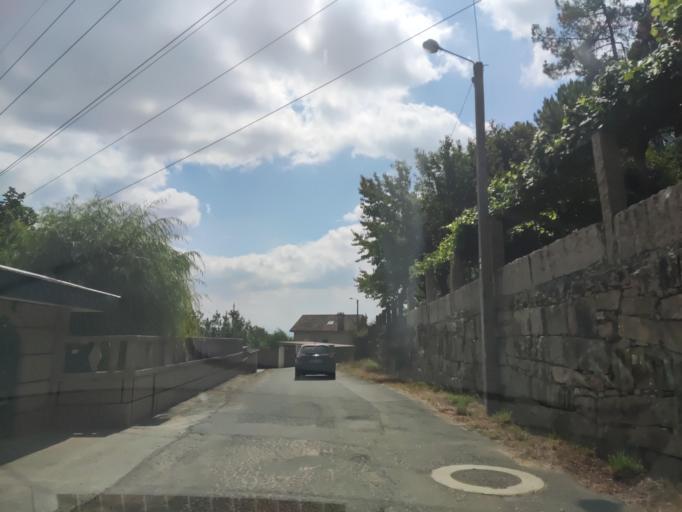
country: ES
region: Galicia
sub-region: Provincia de Pontevedra
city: Porrino
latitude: 42.1535
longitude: -8.6508
